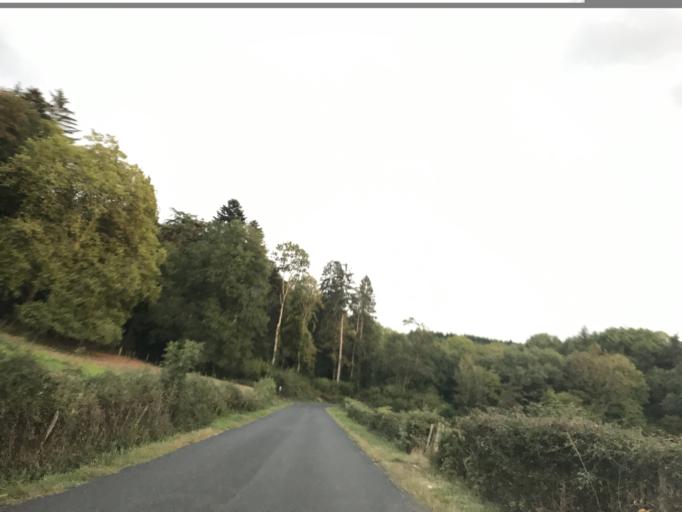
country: FR
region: Auvergne
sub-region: Departement du Puy-de-Dome
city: Escoutoux
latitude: 45.8331
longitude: 3.5519
